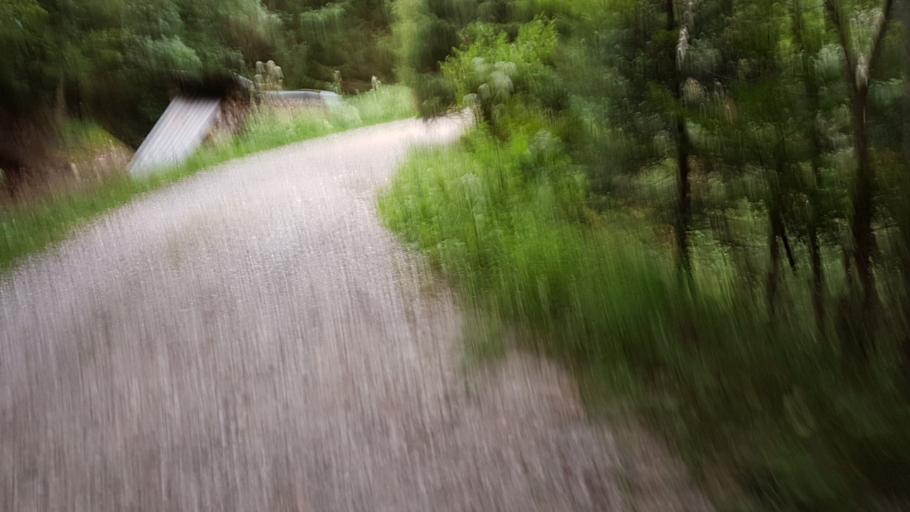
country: CH
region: Lucerne
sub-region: Entlebuch District
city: Oberdiessbach
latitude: 46.8584
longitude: 7.6365
